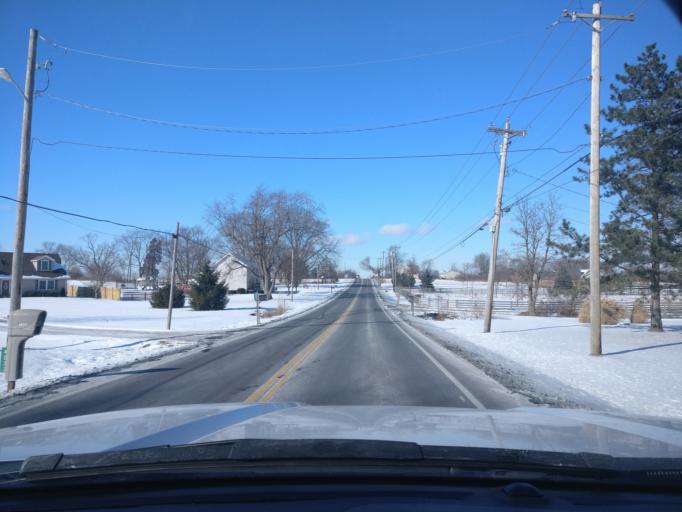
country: US
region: Ohio
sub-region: Warren County
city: Hunter
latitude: 39.4984
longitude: -84.2577
